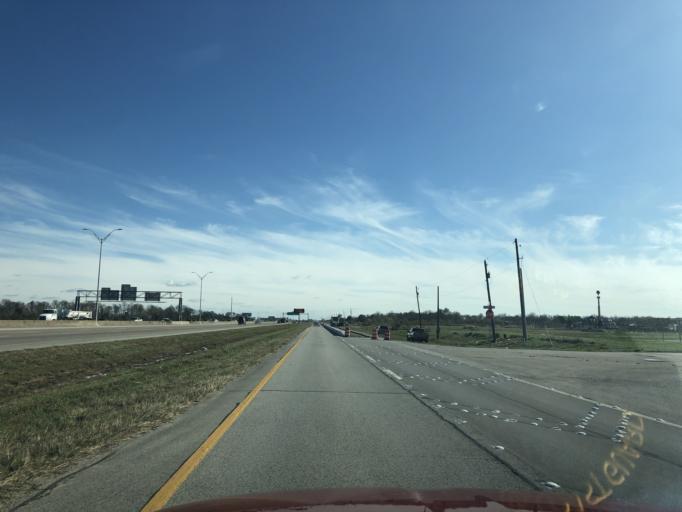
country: US
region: Texas
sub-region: Galveston County
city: Dickinson
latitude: 29.4254
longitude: -95.0557
